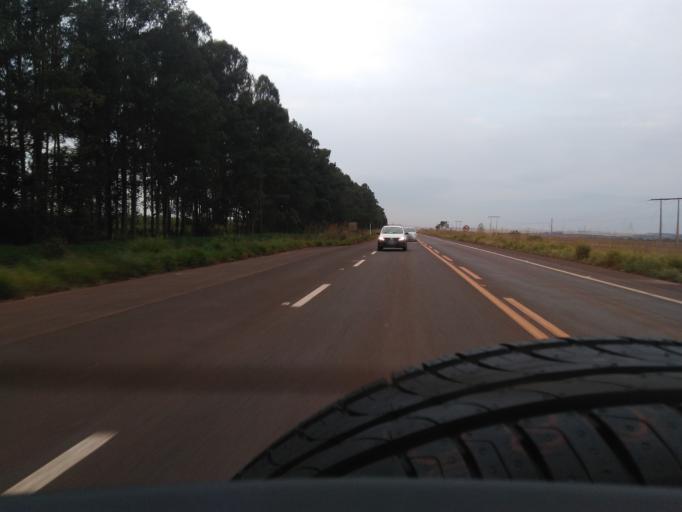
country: BR
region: Mato Grosso do Sul
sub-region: Dourados
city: Dourados
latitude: -22.3010
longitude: -55.0979
